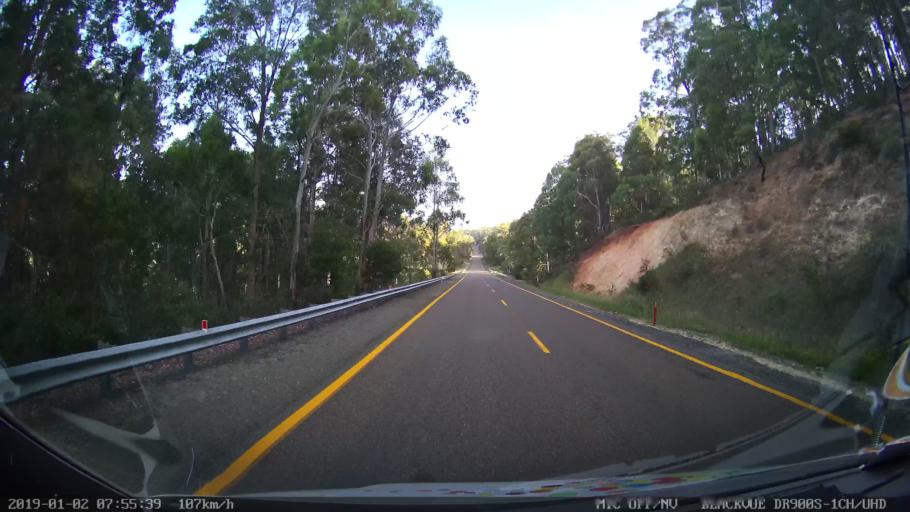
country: AU
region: New South Wales
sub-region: Tumut Shire
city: Tumut
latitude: -35.6815
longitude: 148.4865
